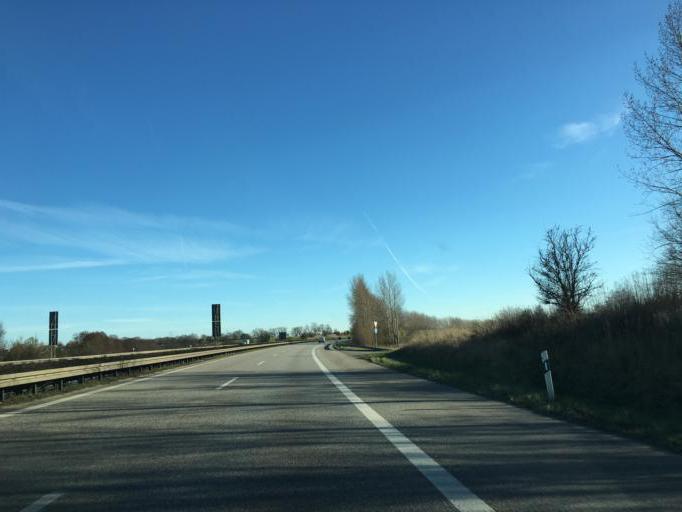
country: DE
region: Mecklenburg-Vorpommern
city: Bentwisch
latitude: 54.0983
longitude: 12.2000
